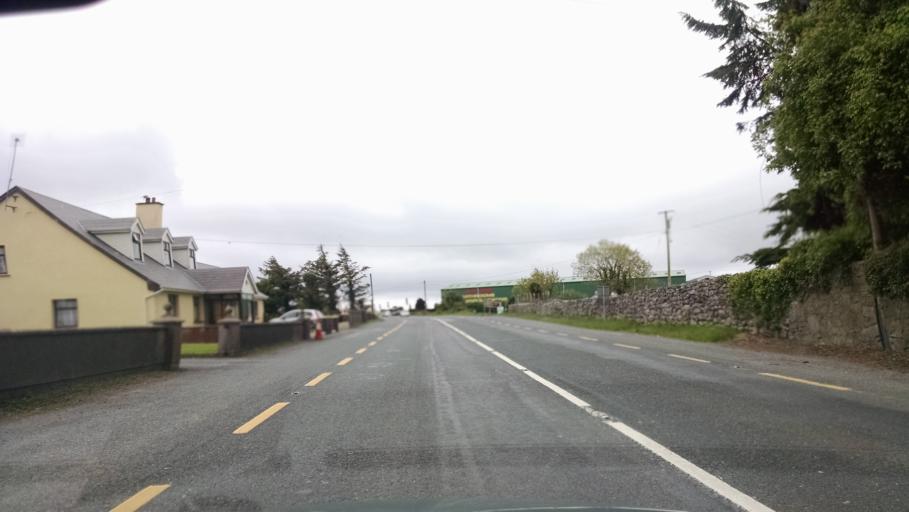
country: IE
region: Connaught
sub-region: County Galway
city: Moycullen
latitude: 53.4650
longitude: -9.1046
